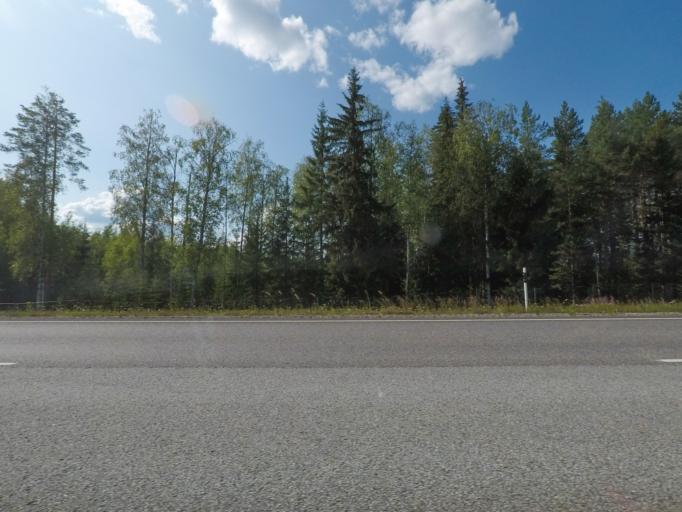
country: FI
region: Southern Savonia
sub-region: Pieksaemaeki
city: Juva
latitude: 61.8049
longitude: 27.6010
